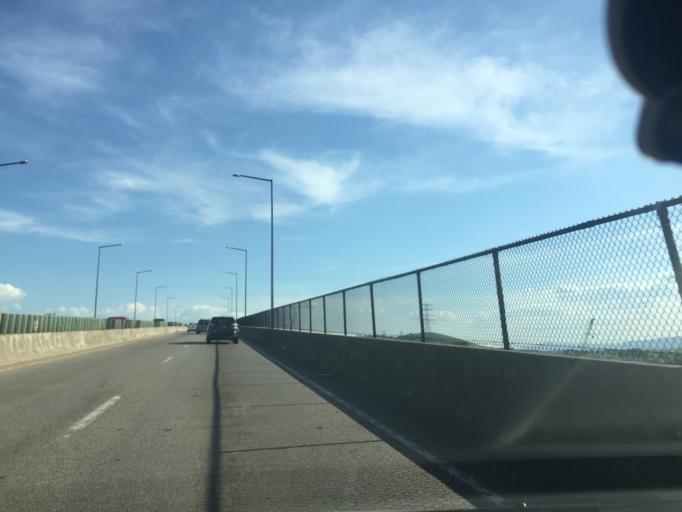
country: US
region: Tennessee
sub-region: Hamilton County
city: East Chattanooga
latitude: 35.1086
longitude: -85.2294
